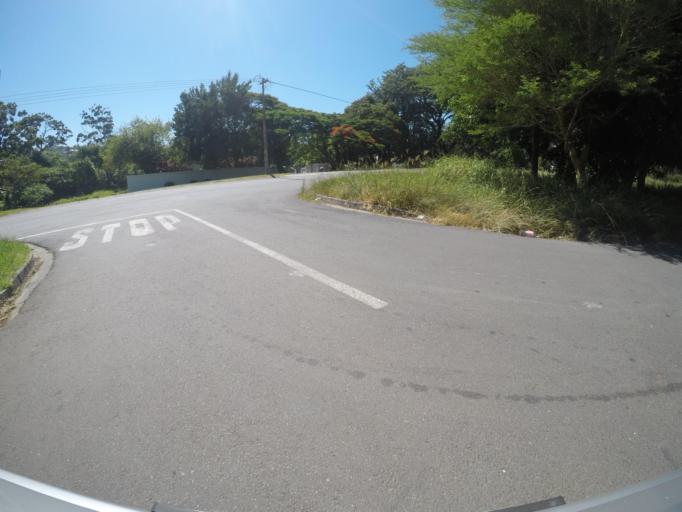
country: ZA
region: Eastern Cape
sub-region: Buffalo City Metropolitan Municipality
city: East London
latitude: -32.9728
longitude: 27.9237
